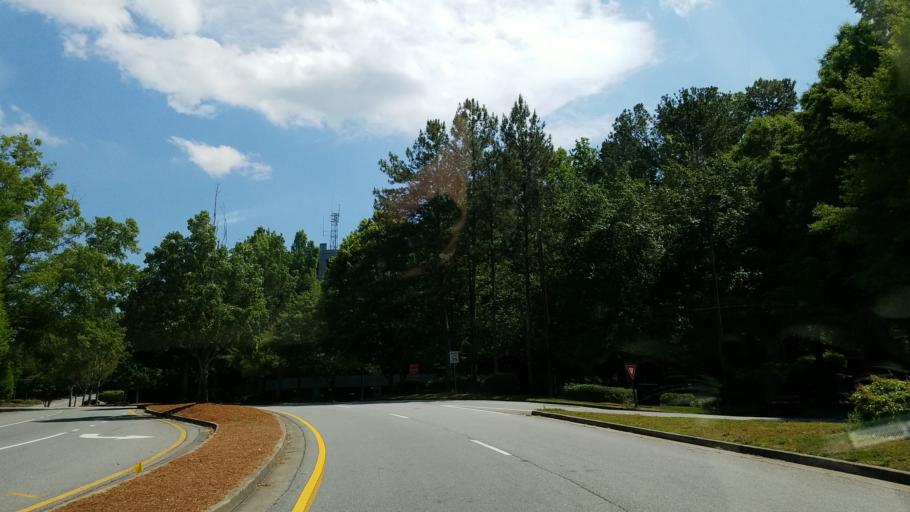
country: US
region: Georgia
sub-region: DeKalb County
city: Dunwoody
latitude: 33.9292
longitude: -84.3344
